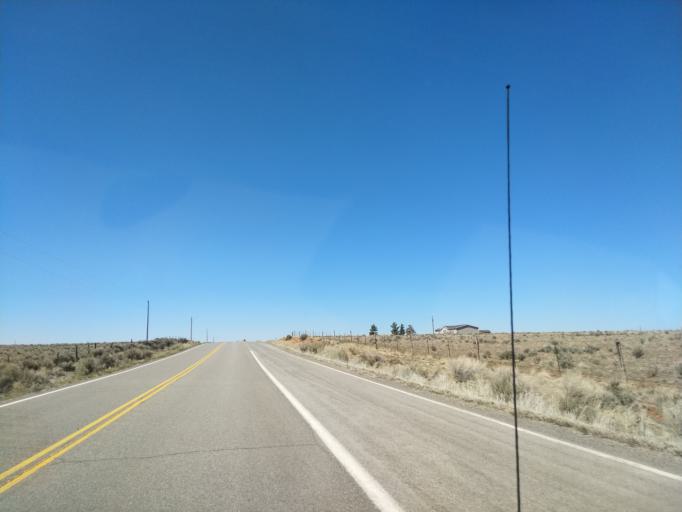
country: US
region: Colorado
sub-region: Mesa County
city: Redlands
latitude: 38.9937
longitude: -108.7466
